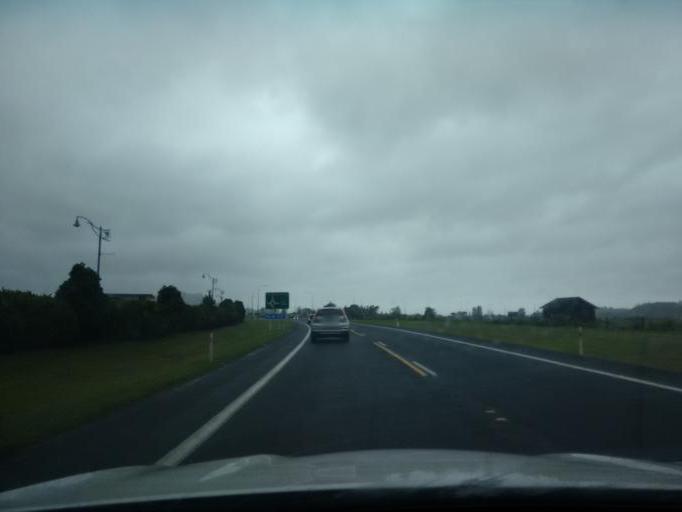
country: NZ
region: Waikato
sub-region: Thames-Coromandel District
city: Whitianga
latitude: -36.8315
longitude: 175.6824
